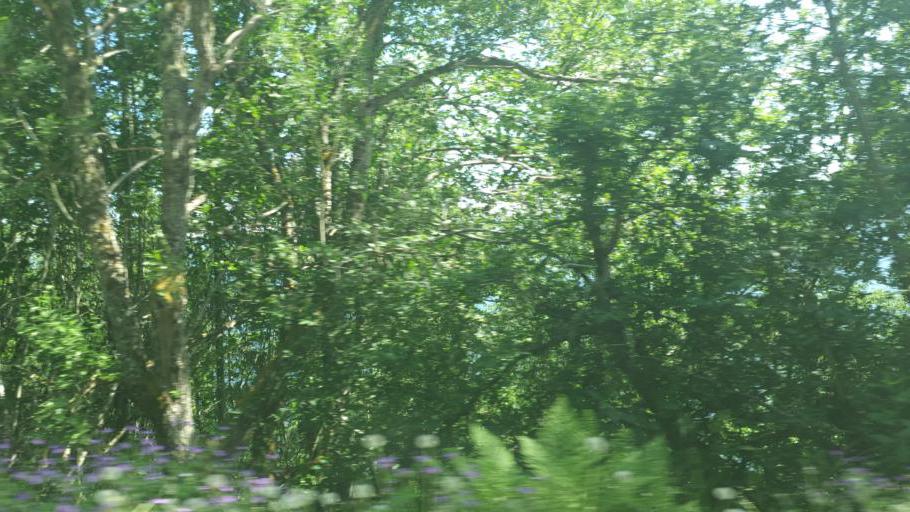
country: NO
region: Nord-Trondelag
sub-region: Leksvik
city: Leksvik
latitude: 63.6933
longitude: 10.6965
